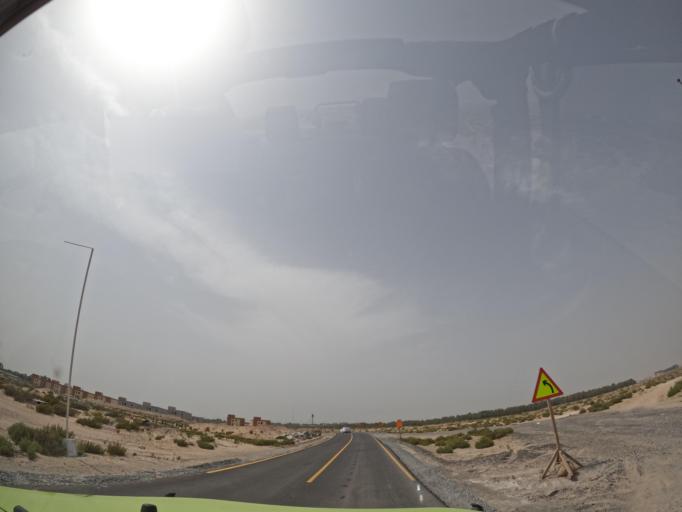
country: AE
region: Dubai
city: Dubai
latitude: 25.1306
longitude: 55.3406
